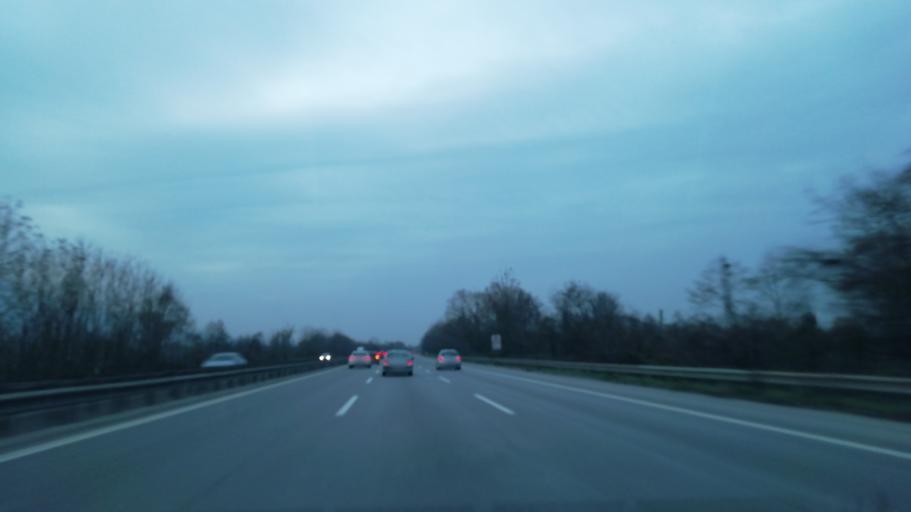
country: TR
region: Sakarya
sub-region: Merkez
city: Sapanca
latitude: 40.7043
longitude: 30.1939
